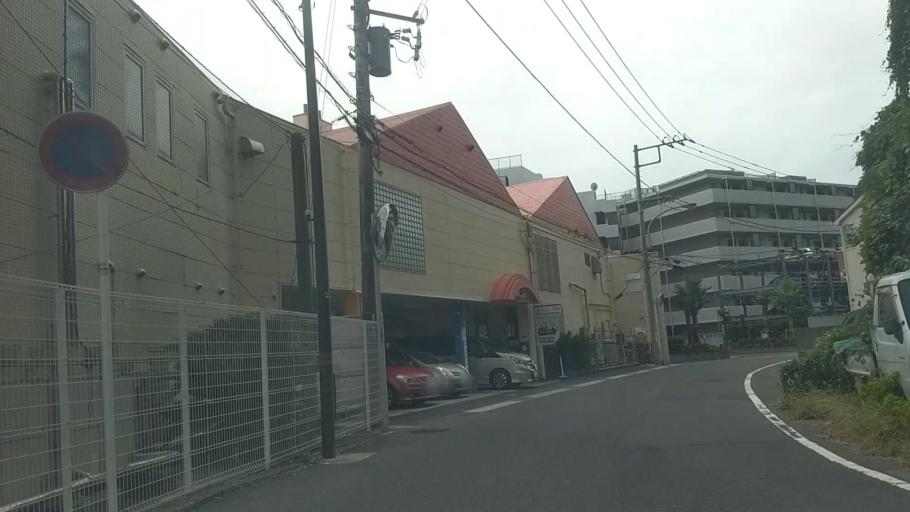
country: JP
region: Kanagawa
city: Yokosuka
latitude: 35.2406
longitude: 139.7245
